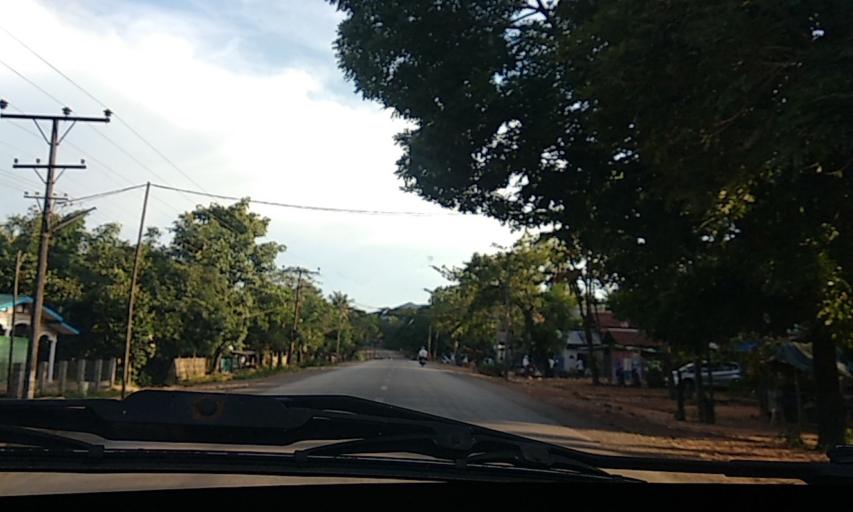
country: MM
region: Mon
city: Mawlamyine
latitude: 16.4047
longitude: 97.7019
